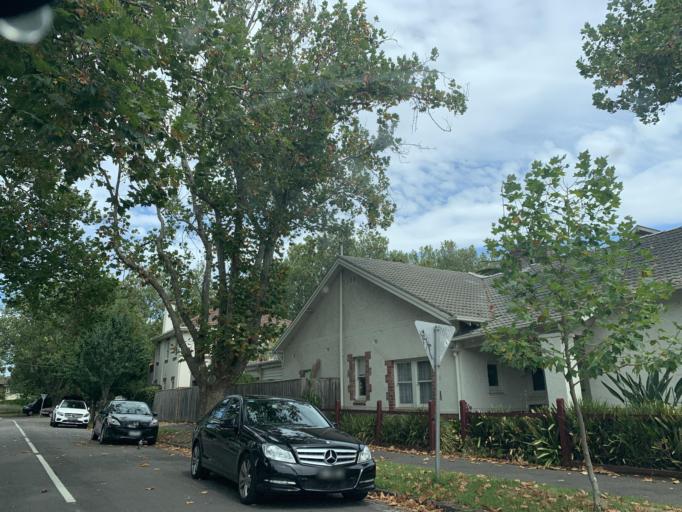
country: AU
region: Victoria
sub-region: Port Phillip
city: Elwood
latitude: -37.8771
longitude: 144.9849
